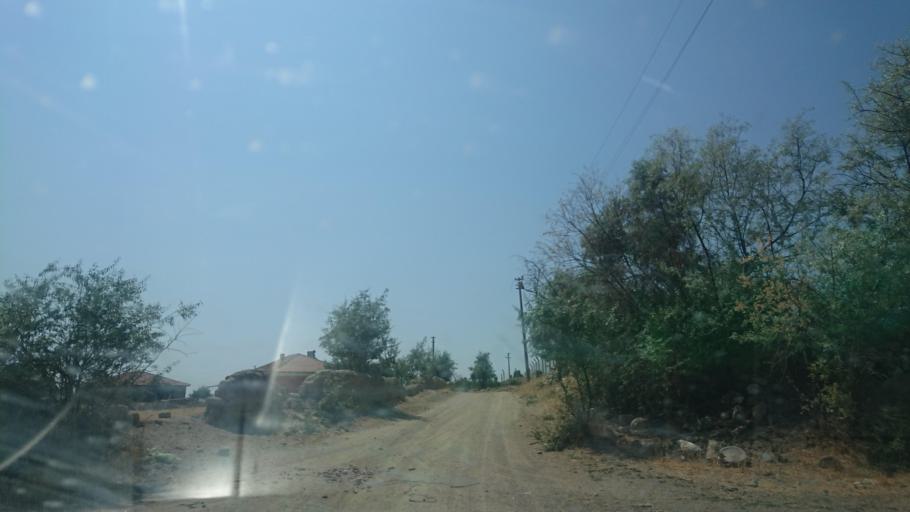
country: TR
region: Aksaray
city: Agacoren
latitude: 38.9359
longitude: 33.9502
